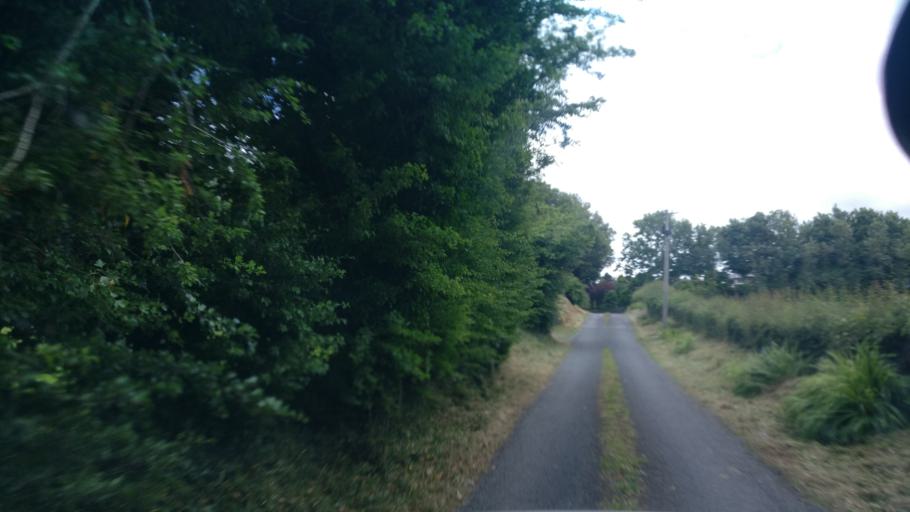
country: IE
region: Connaught
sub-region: County Galway
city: Loughrea
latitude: 53.1709
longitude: -8.5584
